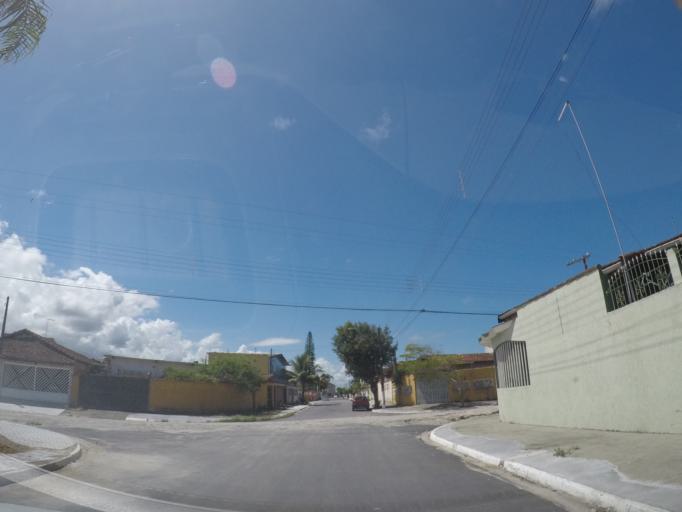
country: BR
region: Sao Paulo
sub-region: Mongagua
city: Mongagua
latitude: -24.0644
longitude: -46.5626
